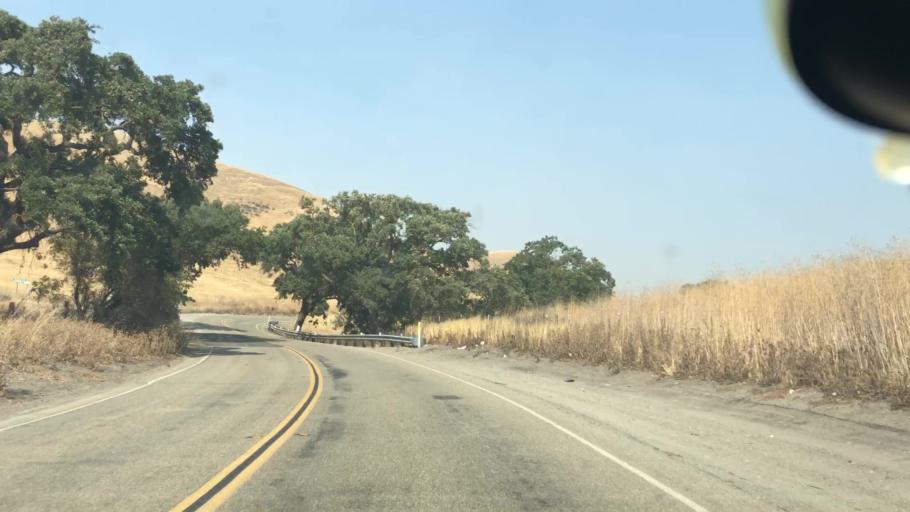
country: US
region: California
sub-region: Alameda County
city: Livermore
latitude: 37.6444
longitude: -121.6308
